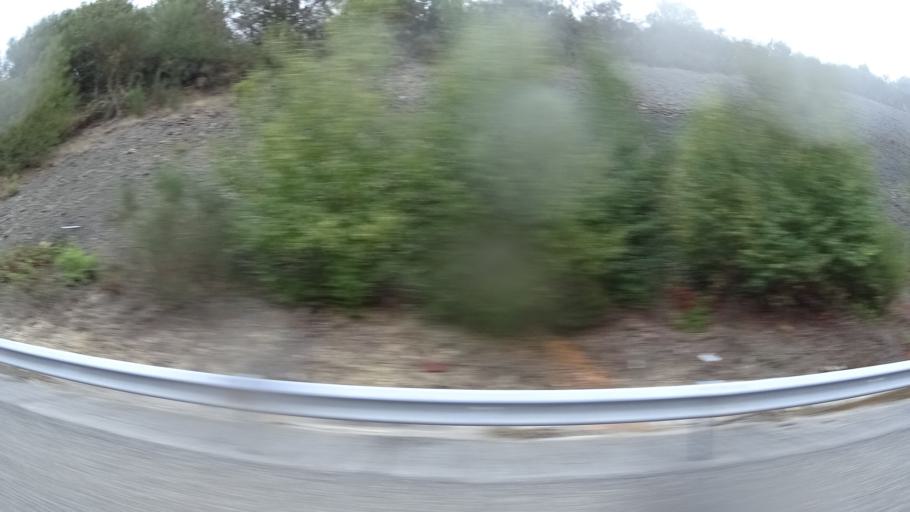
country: ES
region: Galicia
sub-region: Provincia de Lugo
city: Becerrea
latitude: 42.8437
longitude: -7.1195
